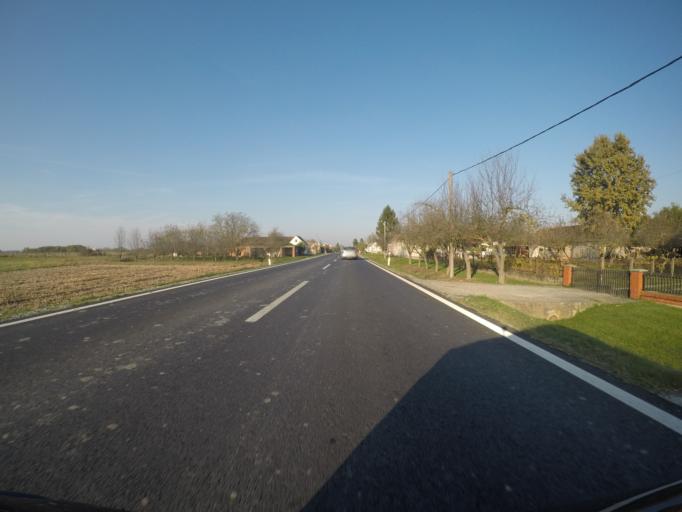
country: HU
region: Somogy
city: Barcs
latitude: 45.9235
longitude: 17.4538
